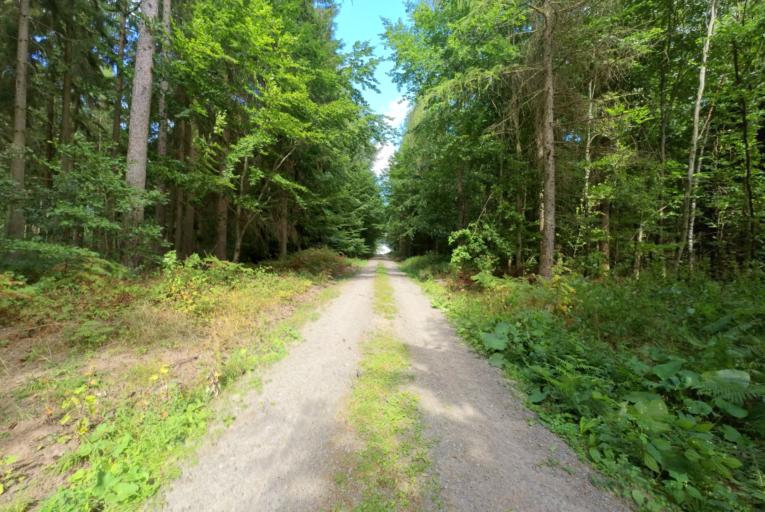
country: DE
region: Baden-Wuerttemberg
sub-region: Karlsruhe Region
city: Fahrenbach
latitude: 49.4235
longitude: 9.1308
